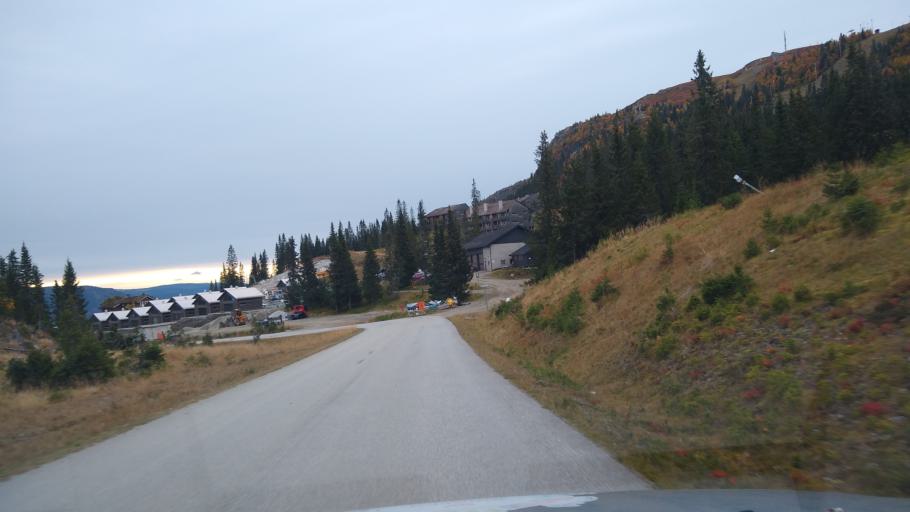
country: NO
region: Oppland
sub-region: Ringebu
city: Ringebu
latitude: 61.4745
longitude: 10.1292
